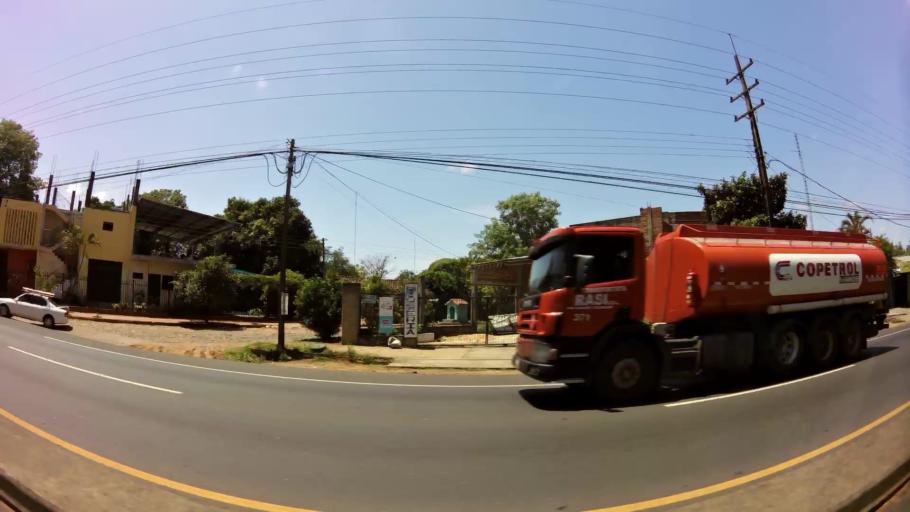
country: PY
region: Central
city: San Antonio
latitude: -25.4149
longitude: -57.5400
